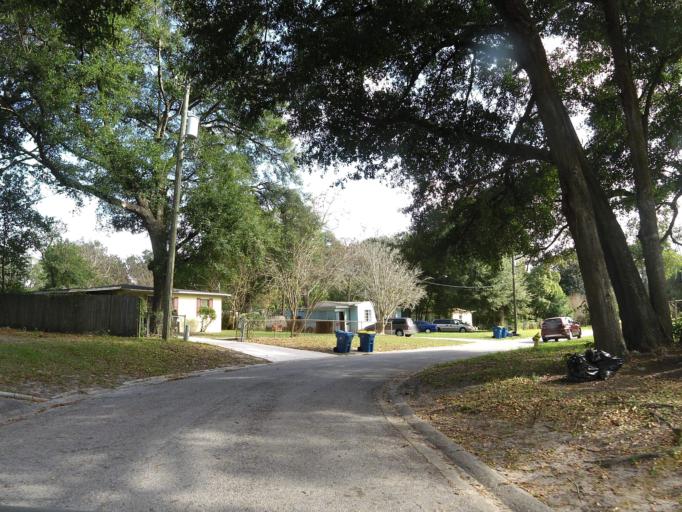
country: US
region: Florida
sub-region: Duval County
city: Jacksonville
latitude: 30.3380
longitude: -81.5882
